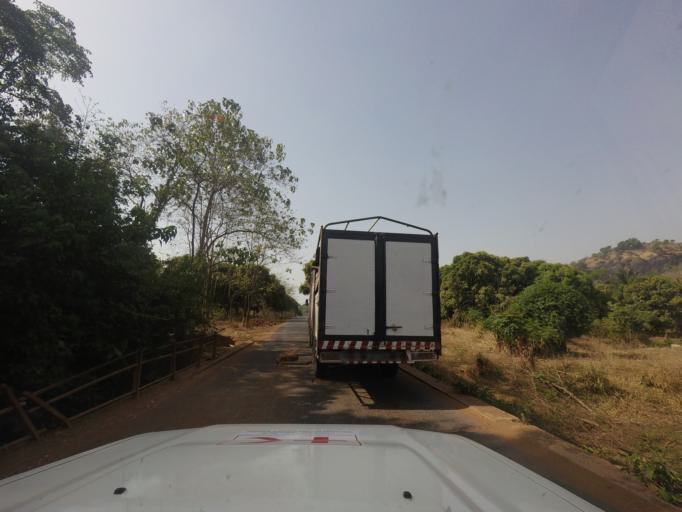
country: GN
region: Mamou
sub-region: Mamou Prefecture
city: Mamou
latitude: 10.2391
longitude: -12.4566
